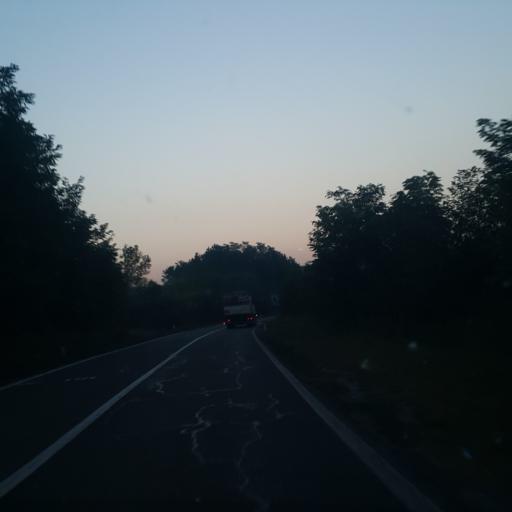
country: RS
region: Central Serbia
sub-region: Nisavski Okrug
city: Svrljig
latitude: 43.4289
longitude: 22.1445
